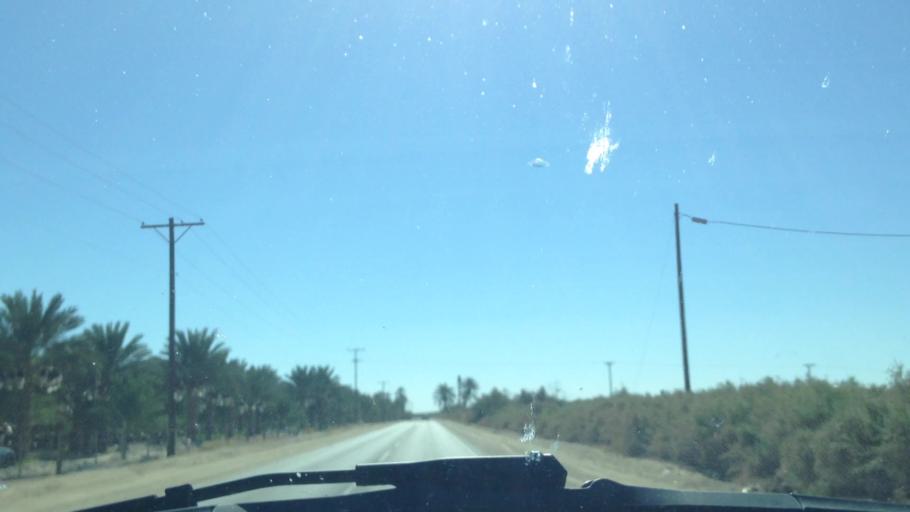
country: US
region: California
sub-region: Riverside County
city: Mecca
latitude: 33.5439
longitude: -116.0368
